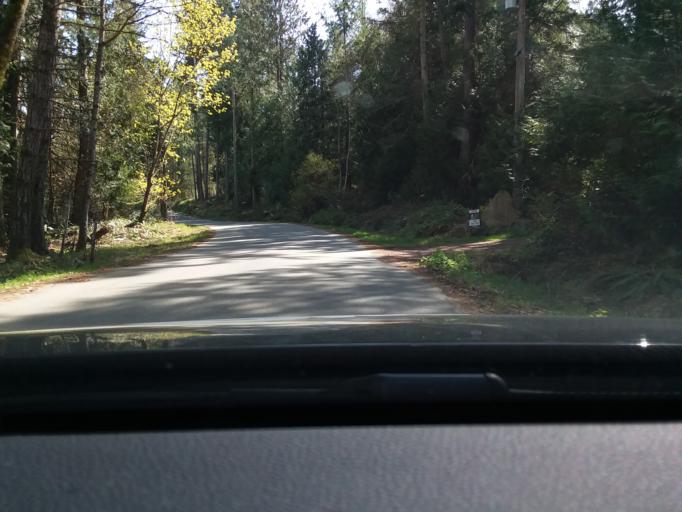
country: CA
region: British Columbia
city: North Saanich
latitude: 48.8501
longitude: -123.4515
